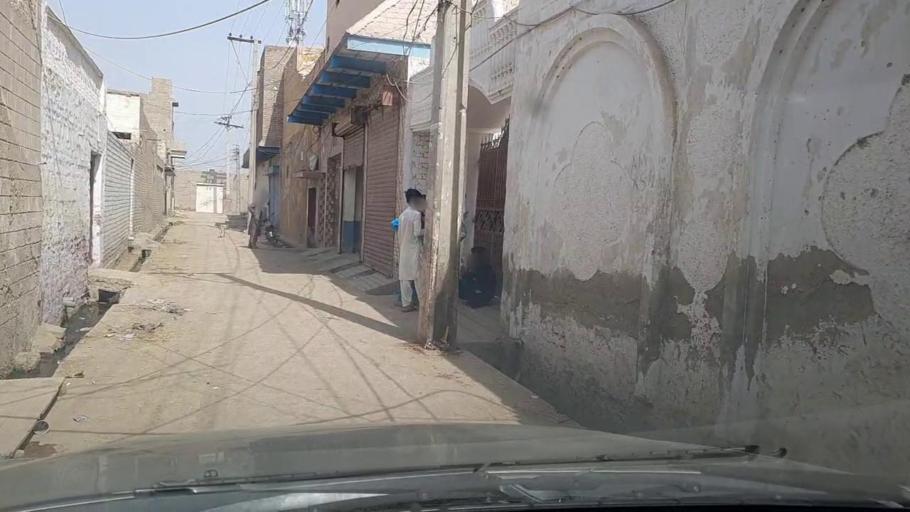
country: PK
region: Sindh
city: Chak
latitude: 27.8291
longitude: 68.7771
